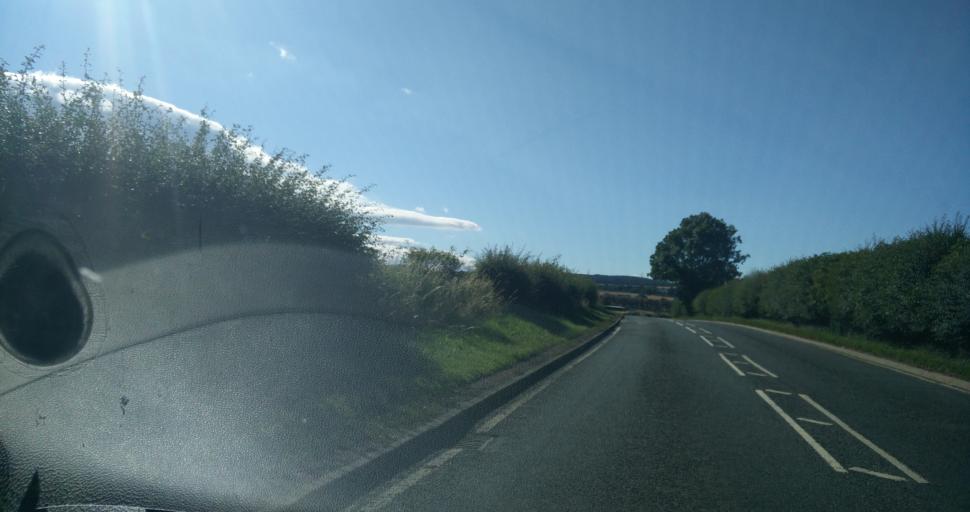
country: GB
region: England
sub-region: County Durham
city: Spennymoor
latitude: 54.7418
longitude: -1.6107
